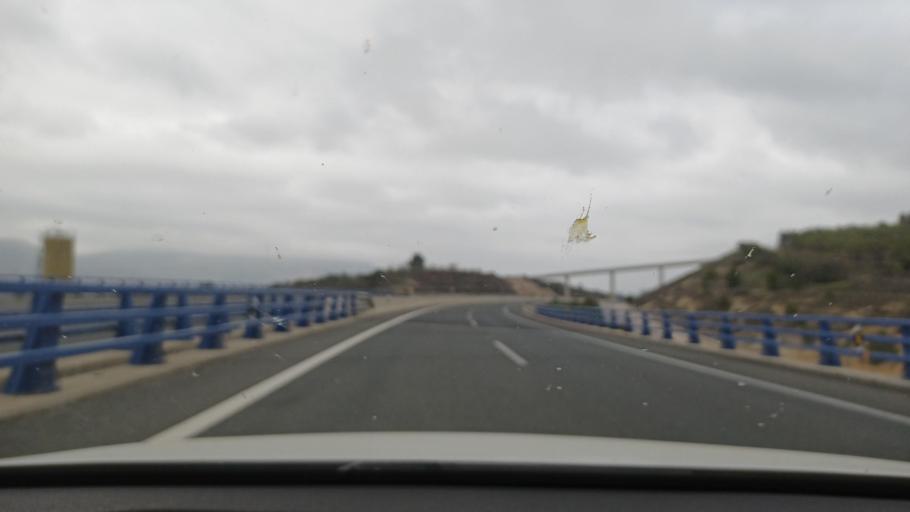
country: ES
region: Valencia
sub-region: Provincia de Alicante
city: Alcoy
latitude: 38.6834
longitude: -0.4610
